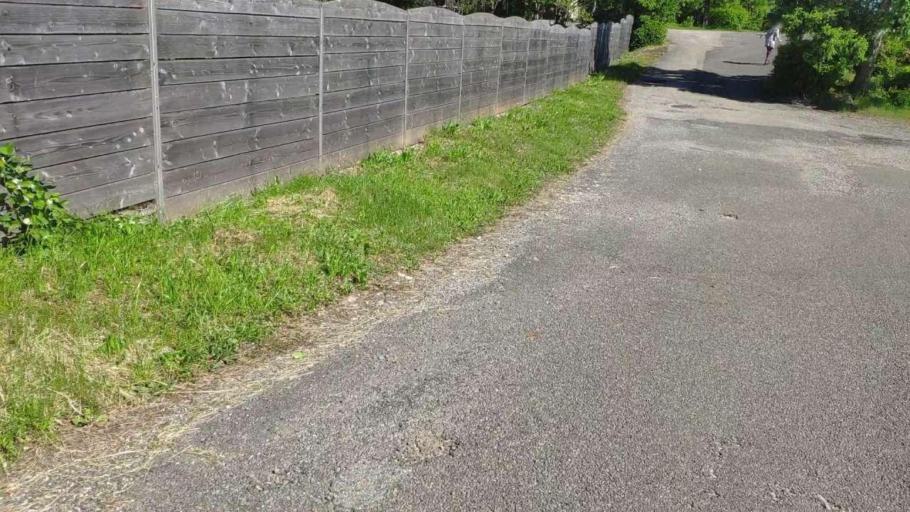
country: FR
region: Franche-Comte
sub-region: Departement du Jura
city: Perrigny
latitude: 46.6886
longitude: 5.6635
